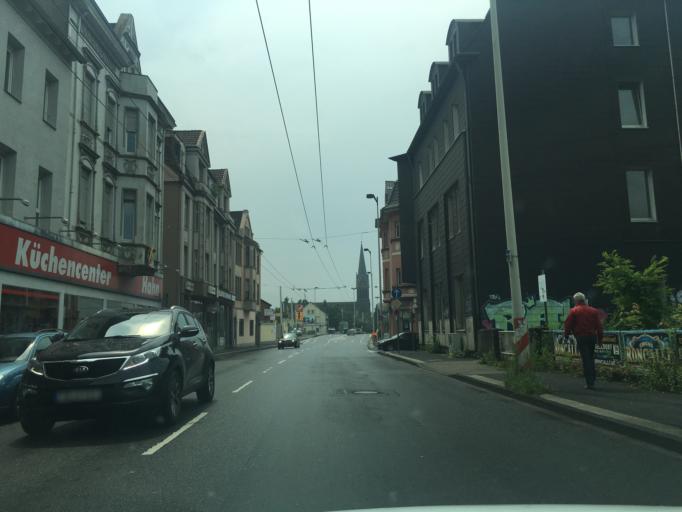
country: DE
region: North Rhine-Westphalia
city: Haan
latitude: 51.1593
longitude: 7.0070
